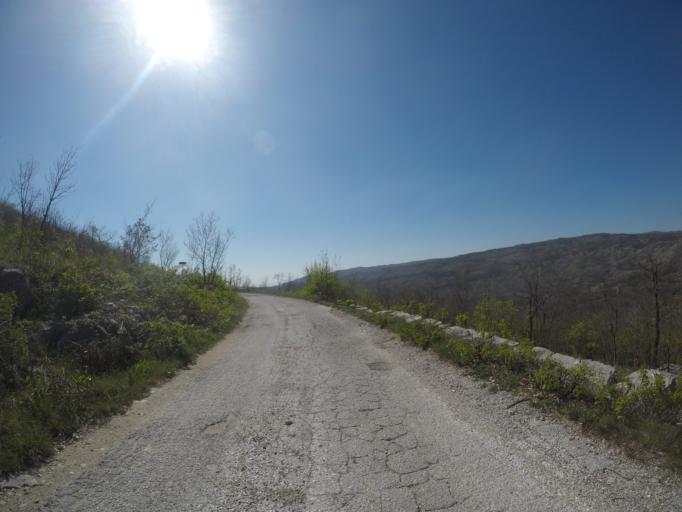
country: ME
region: Danilovgrad
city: Danilovgrad
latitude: 42.5347
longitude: 19.0161
